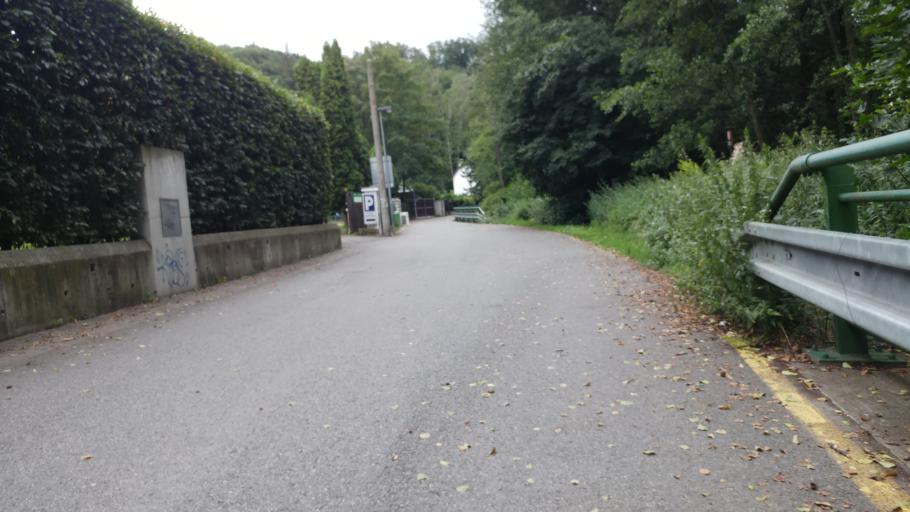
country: CZ
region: Praha
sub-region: Praha 14
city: Hostavice
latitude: 50.0482
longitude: 14.5332
